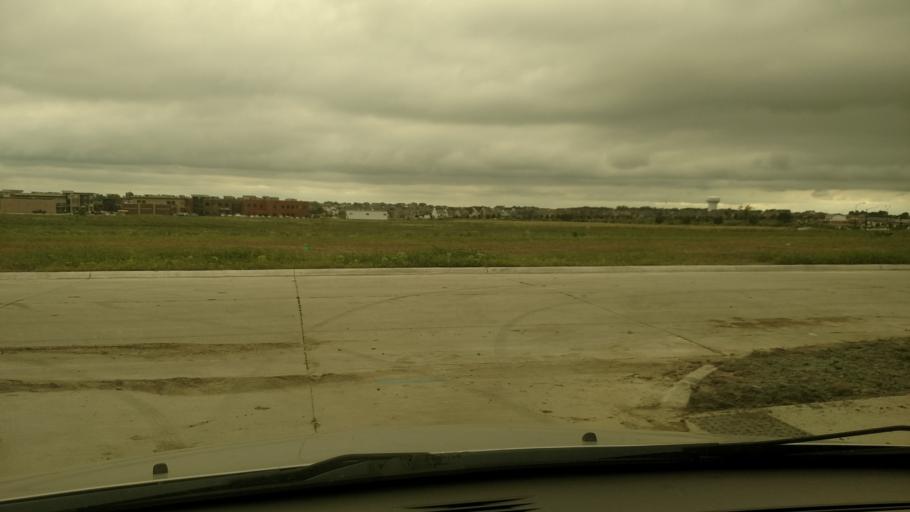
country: US
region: Iowa
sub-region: Polk County
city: Ankeny
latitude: 41.7158
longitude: -93.6157
